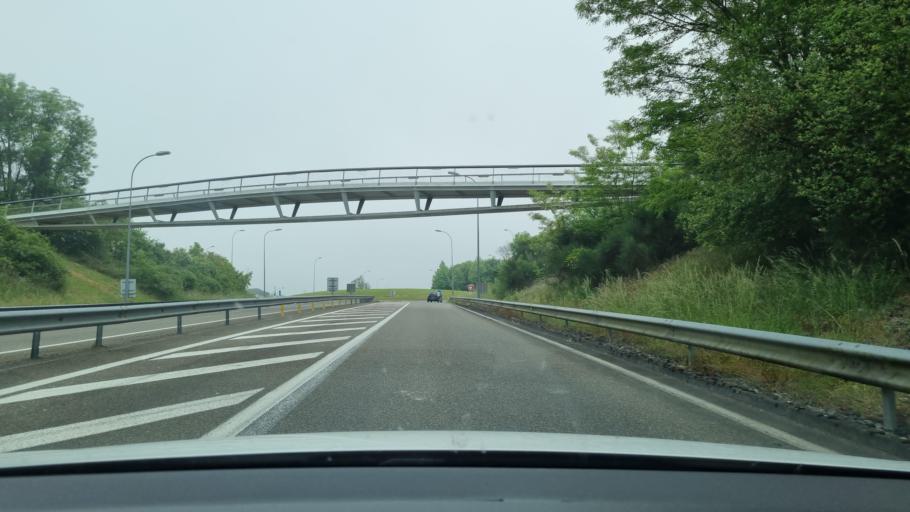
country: FR
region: Aquitaine
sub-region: Departement des Landes
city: Saint-Sever
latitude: 43.7461
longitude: -0.5631
